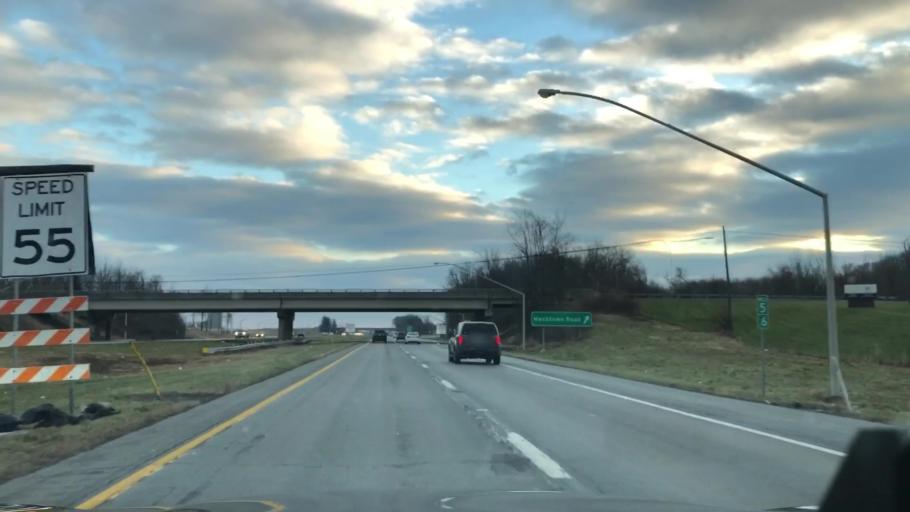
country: US
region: Pennsylvania
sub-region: Northampton County
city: Palmer Heights
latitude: 40.7052
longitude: -75.2901
